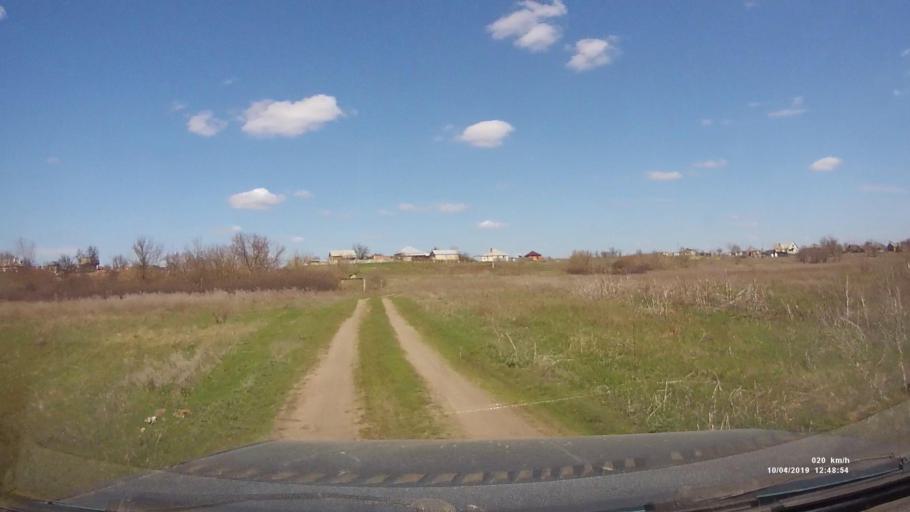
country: RU
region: Rostov
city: Kamensk-Shakhtinskiy
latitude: 48.3561
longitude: 40.2238
